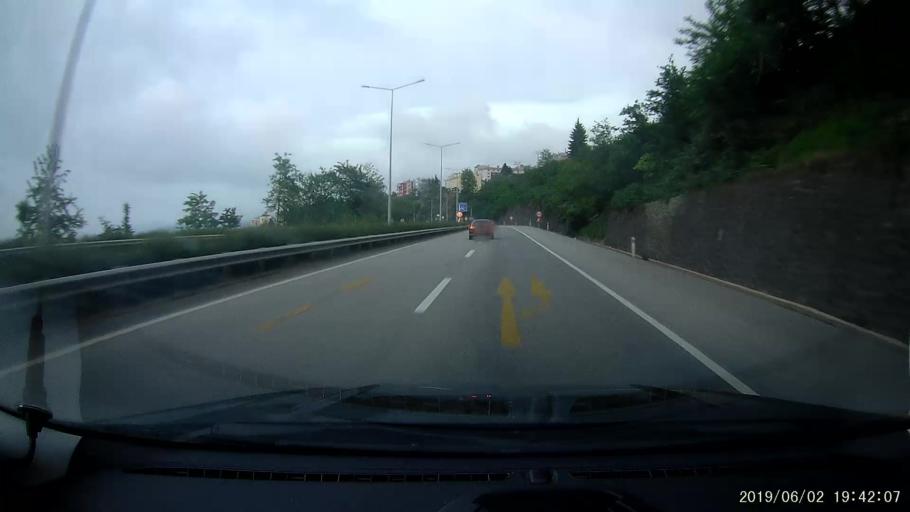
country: TR
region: Giresun
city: Kesap
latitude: 40.9159
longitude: 38.4966
